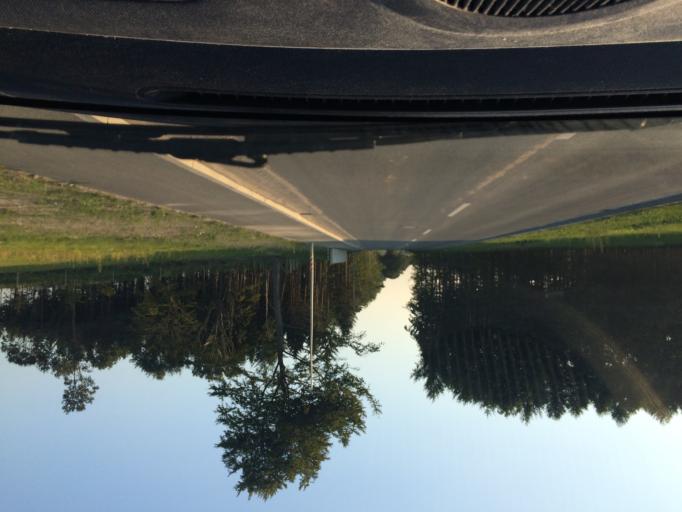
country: DE
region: Lower Saxony
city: Walsrode
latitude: 52.8452
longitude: 9.5557
